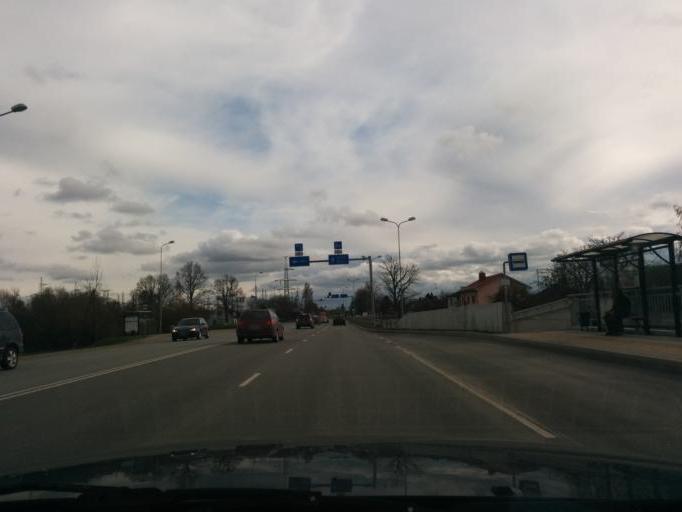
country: LV
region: Jelgava
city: Jelgava
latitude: 56.6317
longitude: 23.7268
